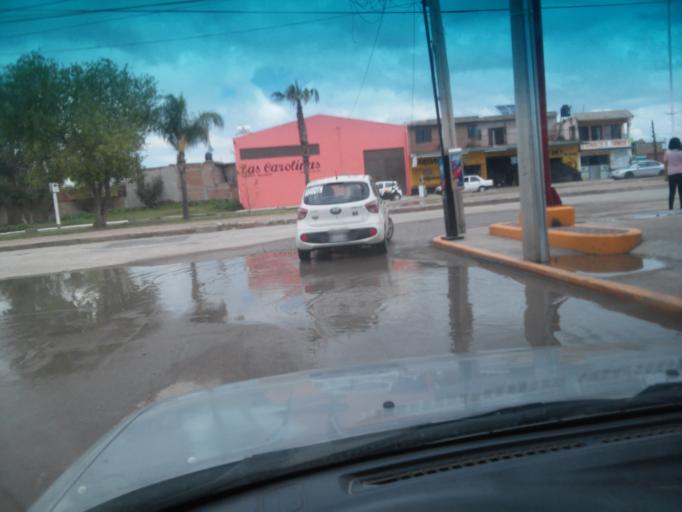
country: MX
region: Durango
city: Victoria de Durango
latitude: 24.0111
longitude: -104.6269
